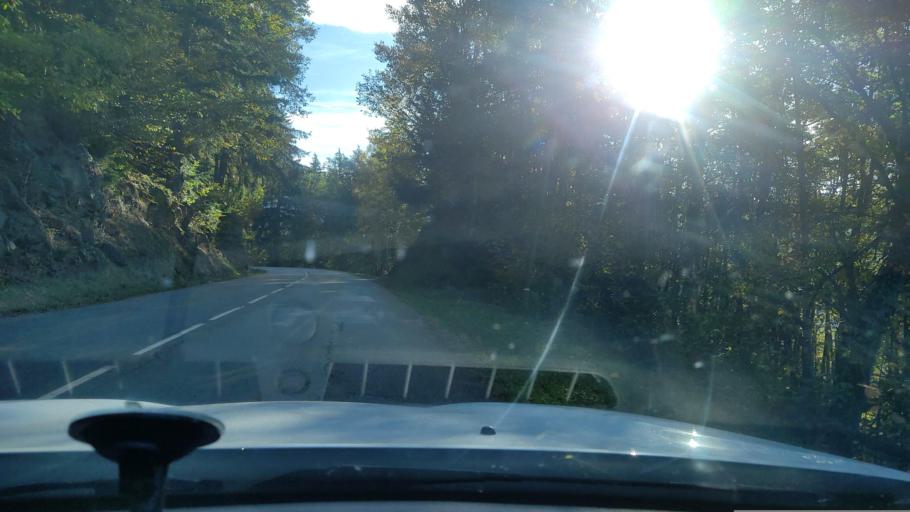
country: FR
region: Rhone-Alpes
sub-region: Departement de la Savoie
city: Beaufort
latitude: 45.7336
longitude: 6.5485
